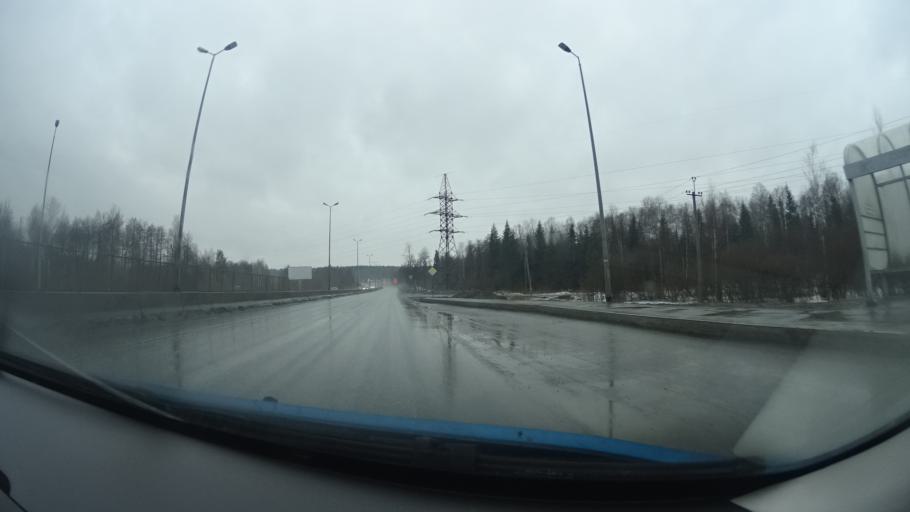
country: RU
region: Perm
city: Kondratovo
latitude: 58.0518
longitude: 56.0665
